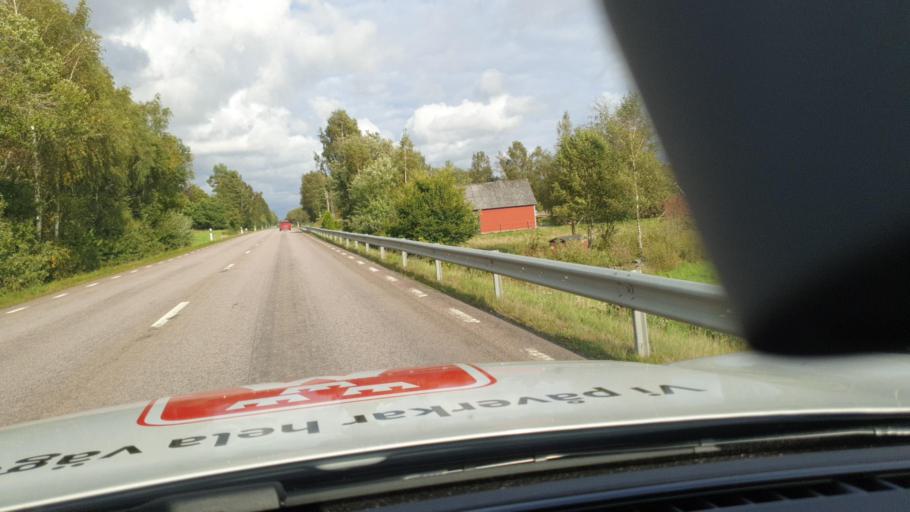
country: SE
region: Skane
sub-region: Angelholms Kommun
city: Munka-Ljungby
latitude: 56.2767
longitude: 13.0288
